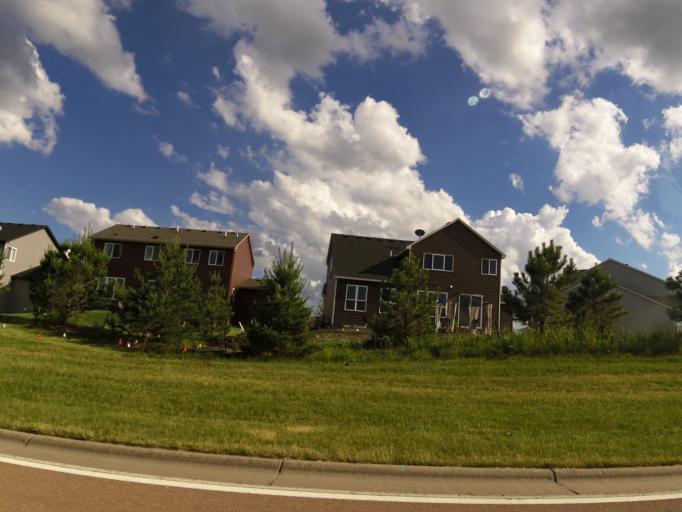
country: US
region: Minnesota
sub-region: Carver County
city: Waconia
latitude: 44.8364
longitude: -93.7813
